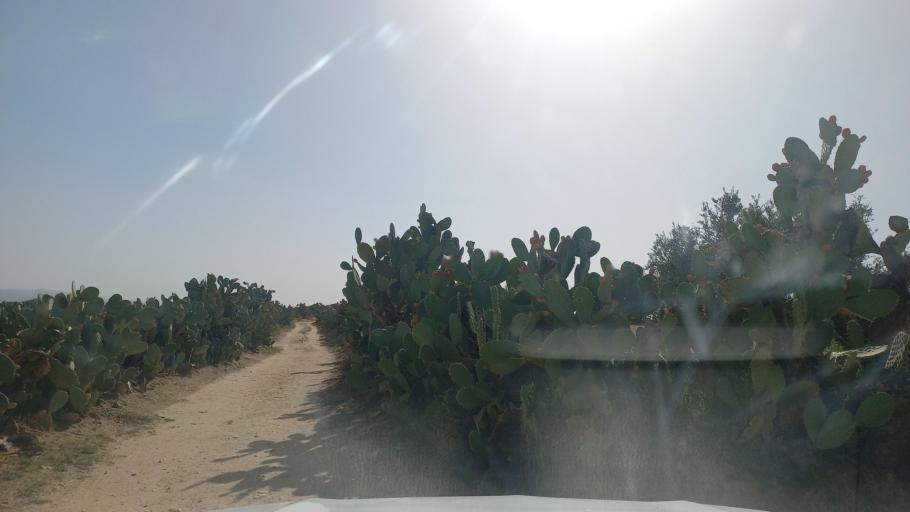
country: TN
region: Al Qasrayn
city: Sbiba
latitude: 35.3179
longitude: 9.0254
